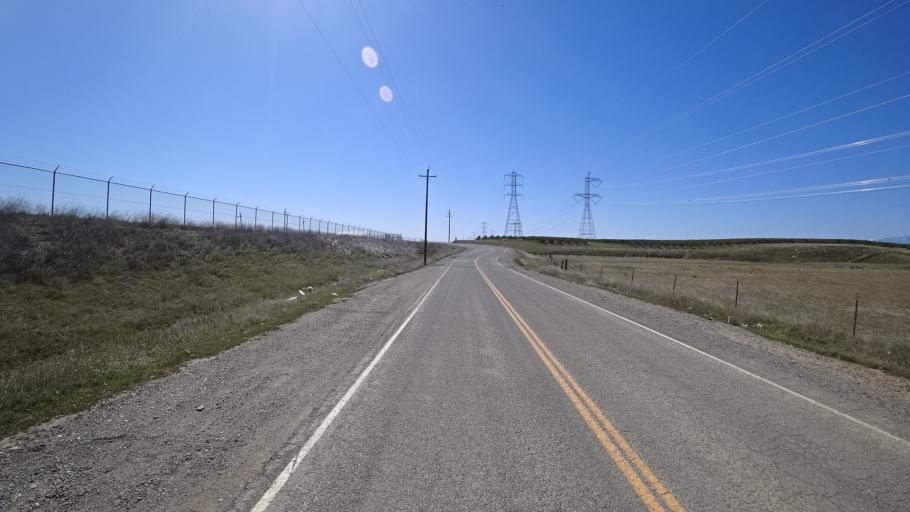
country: US
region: California
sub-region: Glenn County
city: Willows
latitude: 39.6260
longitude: -122.2730
